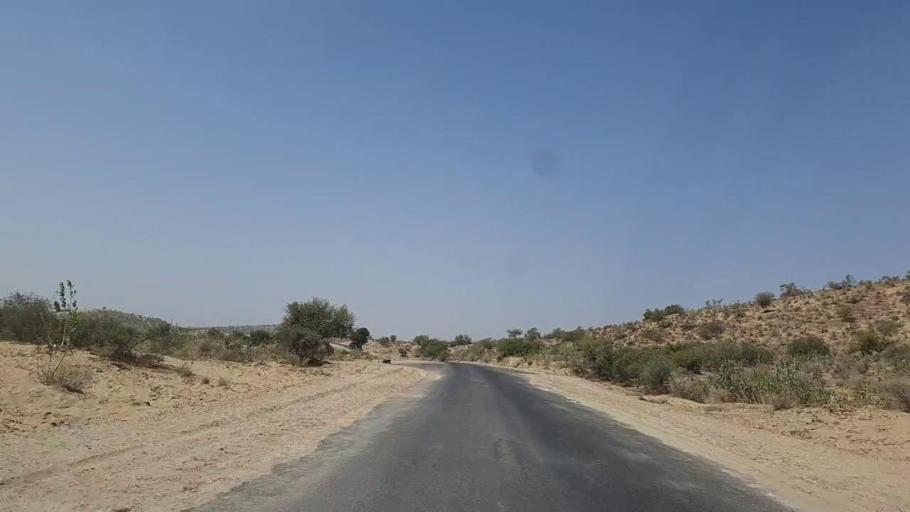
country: PK
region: Sindh
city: Diplo
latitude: 24.5787
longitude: 69.4959
